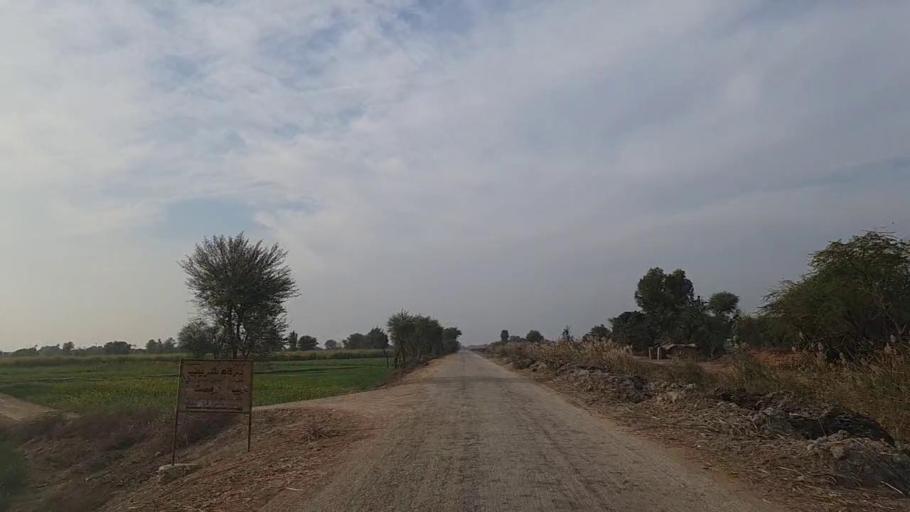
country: PK
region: Sindh
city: Daur
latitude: 26.4951
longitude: 68.4526
